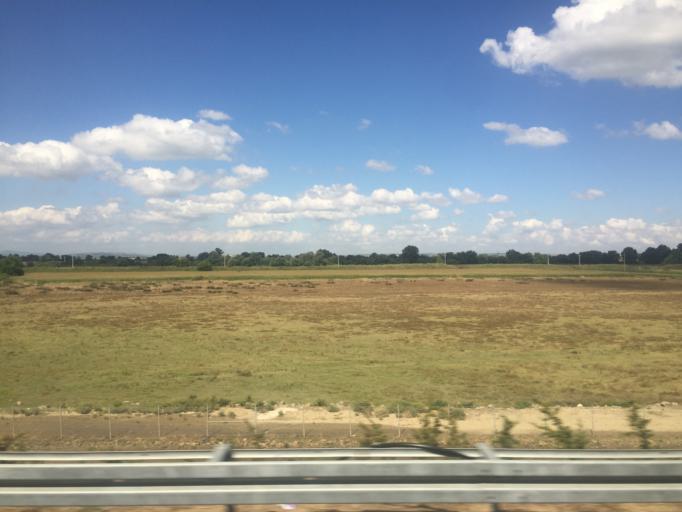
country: TR
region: Bursa
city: Tatkavakli
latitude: 40.1155
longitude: 28.2777
